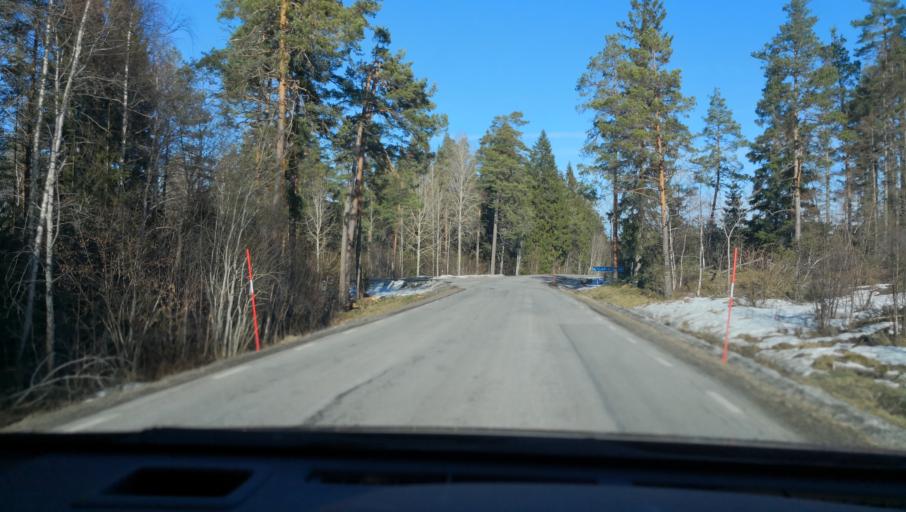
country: SE
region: Uppsala
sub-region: Osthammars Kommun
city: Osterbybruk
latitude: 60.2582
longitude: 17.9482
